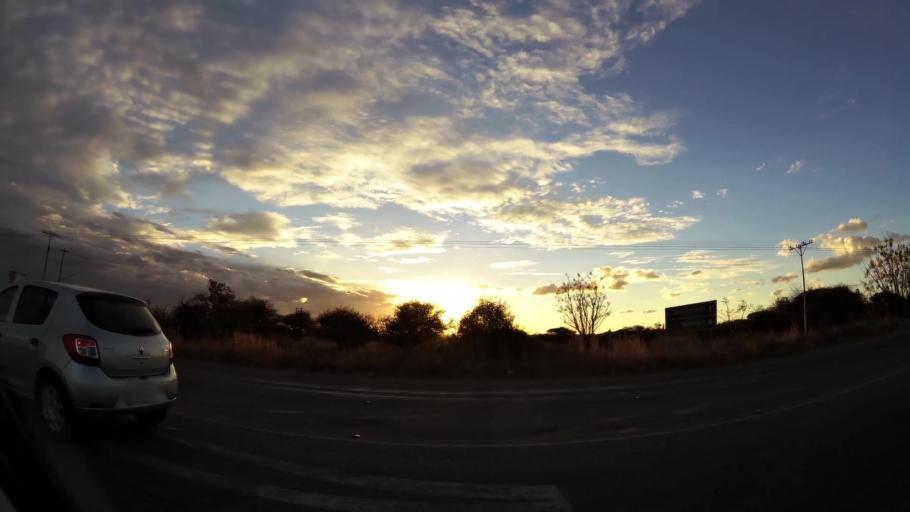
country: ZA
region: Limpopo
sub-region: Capricorn District Municipality
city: Polokwane
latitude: -23.8319
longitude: 29.4893
